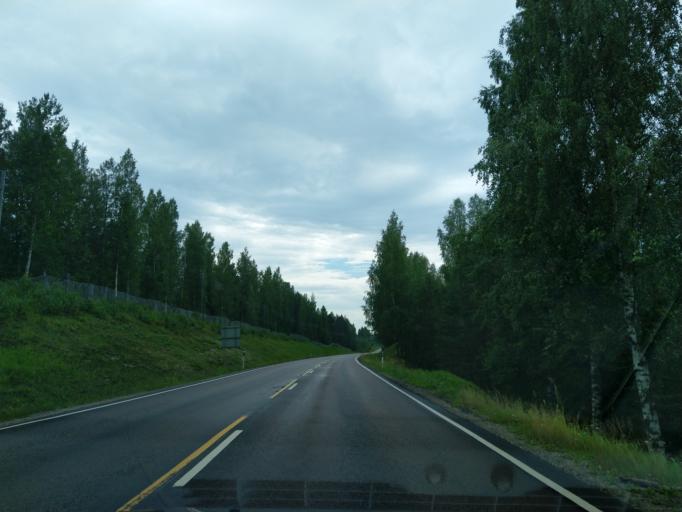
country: FI
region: Southern Savonia
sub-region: Savonlinna
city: Punkaharju
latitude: 61.6856
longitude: 29.4189
